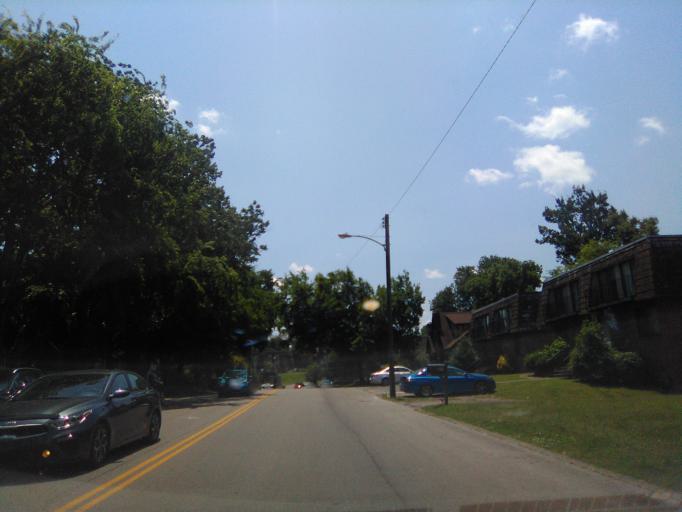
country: US
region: Tennessee
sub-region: Davidson County
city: Belle Meade
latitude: 36.1317
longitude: -86.8388
